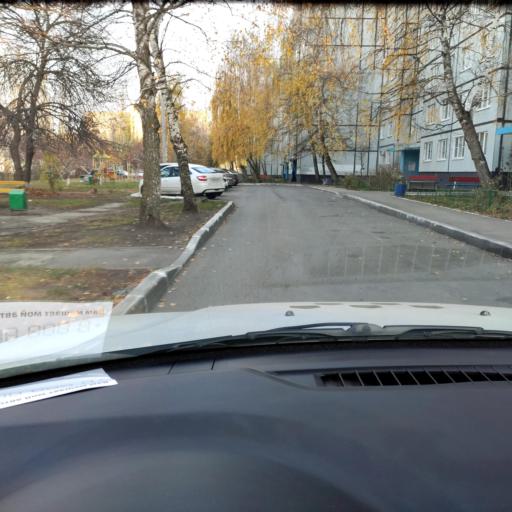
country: RU
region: Samara
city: Tol'yatti
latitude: 53.5085
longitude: 49.4477
